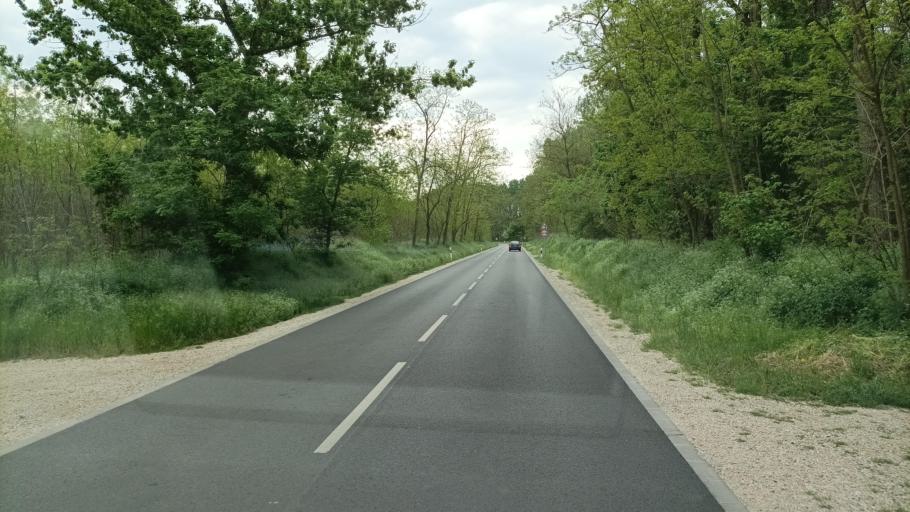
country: HU
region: Pest
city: Nyaregyhaza
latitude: 47.2809
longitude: 19.4652
